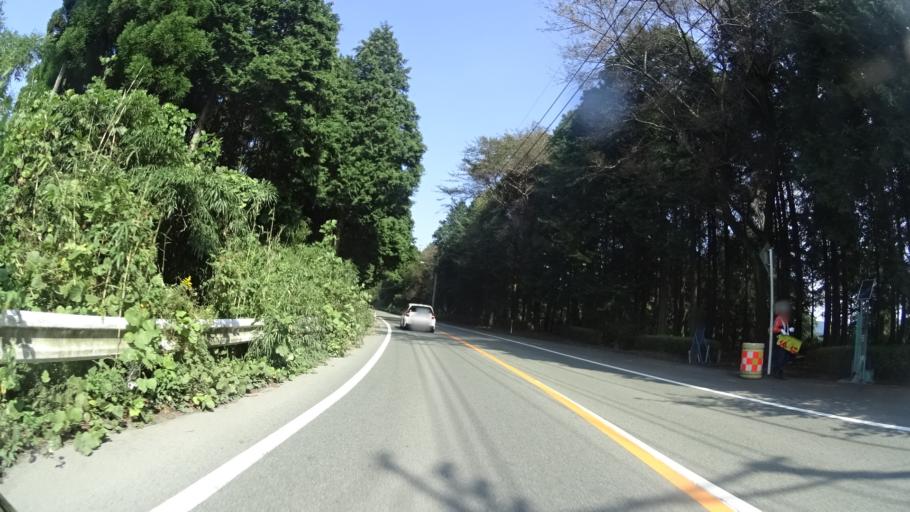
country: JP
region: Kumamoto
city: Ozu
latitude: 32.8957
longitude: 130.9309
